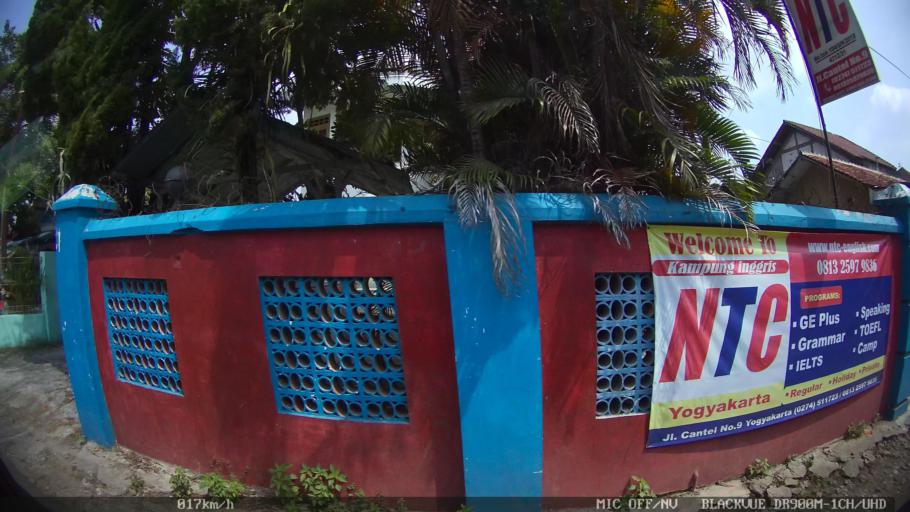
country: ID
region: Daerah Istimewa Yogyakarta
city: Yogyakarta
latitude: -7.7947
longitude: 110.3877
